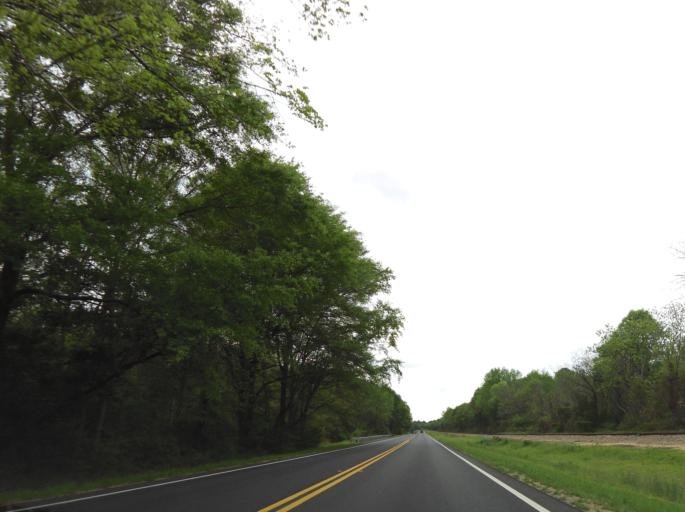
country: US
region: Georgia
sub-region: Laurens County
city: Dublin
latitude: 32.5316
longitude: -82.9185
